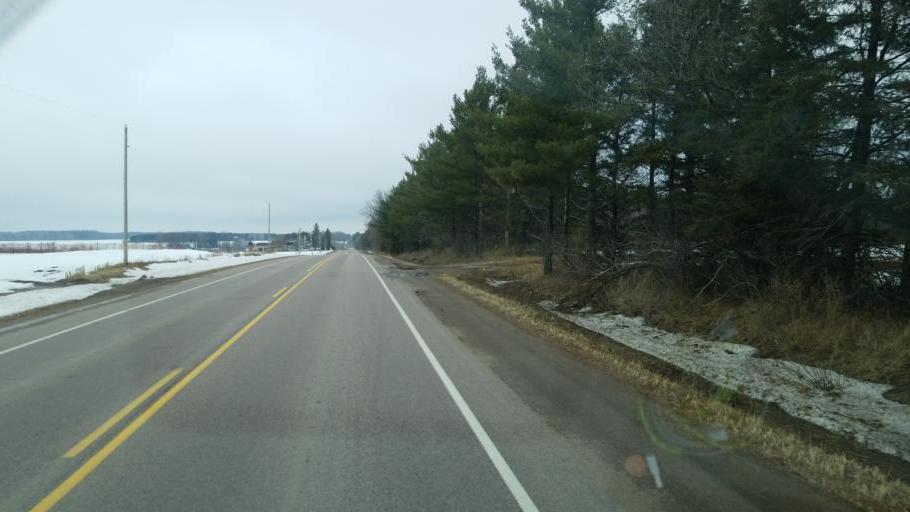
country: US
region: Wisconsin
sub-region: Wood County
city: Marshfield
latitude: 44.6491
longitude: -90.2184
